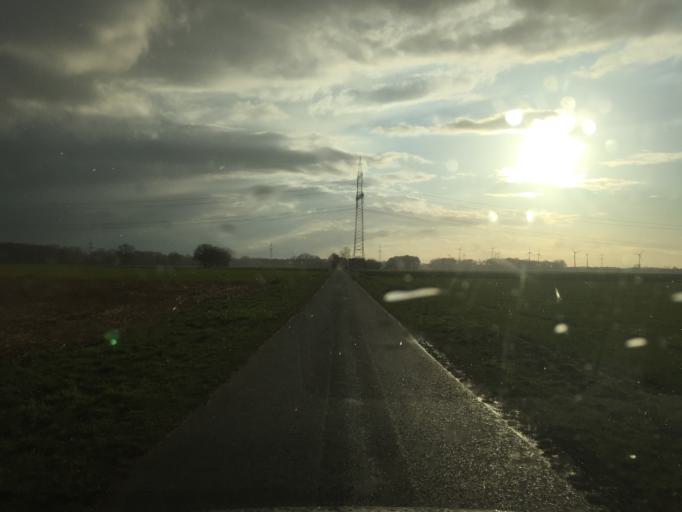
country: DE
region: Lower Saxony
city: Steyerberg
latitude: 52.5491
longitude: 9.0039
